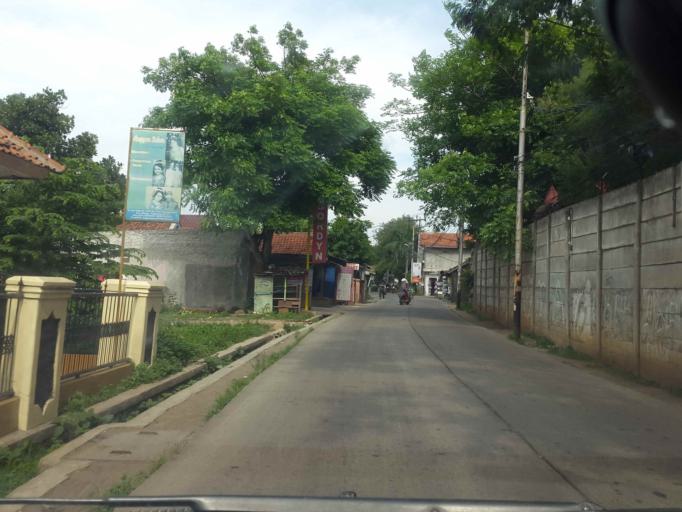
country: ID
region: Banten
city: Tangerang
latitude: -6.2225
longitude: 106.6449
